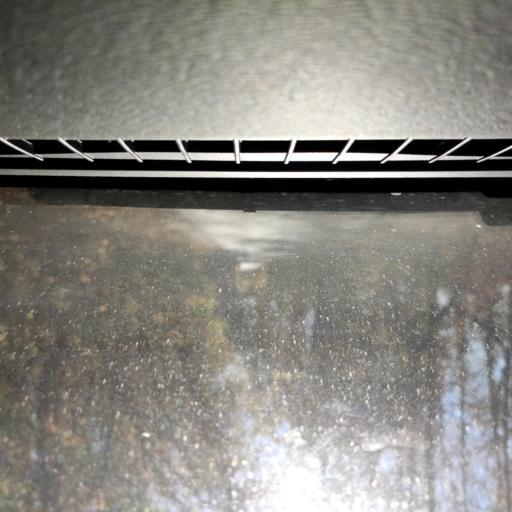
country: RU
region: Voronezj
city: Somovo
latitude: 51.6854
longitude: 39.2995
